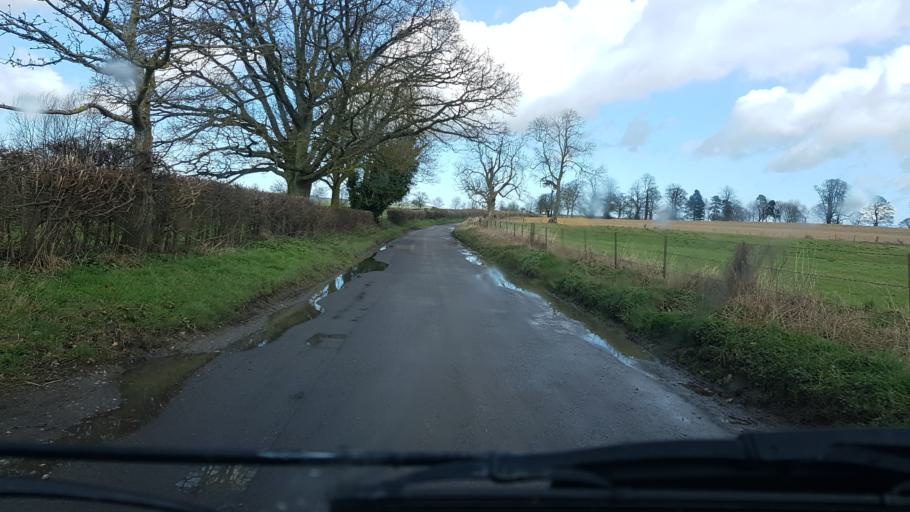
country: GB
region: England
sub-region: Wiltshire
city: Wilsford
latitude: 51.3241
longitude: -1.8705
